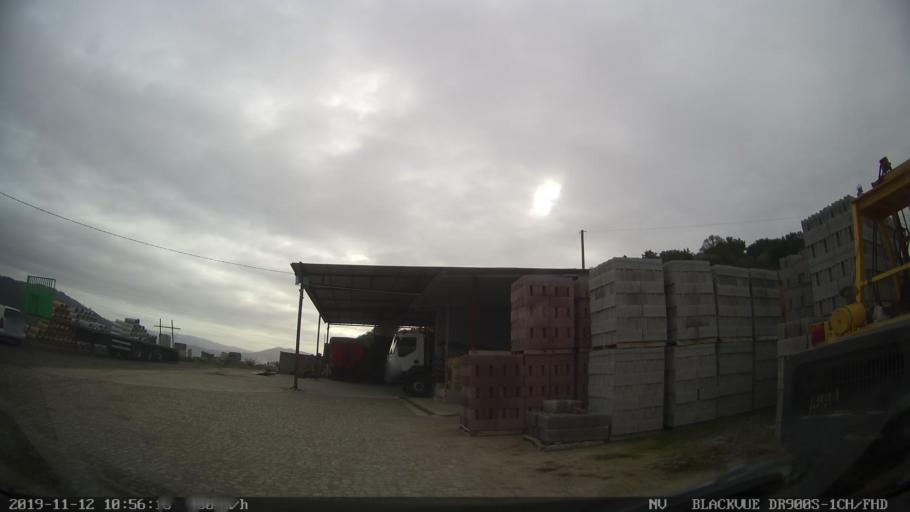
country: PT
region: Vila Real
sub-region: Sabrosa
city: Vilela
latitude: 41.2056
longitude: -7.5279
